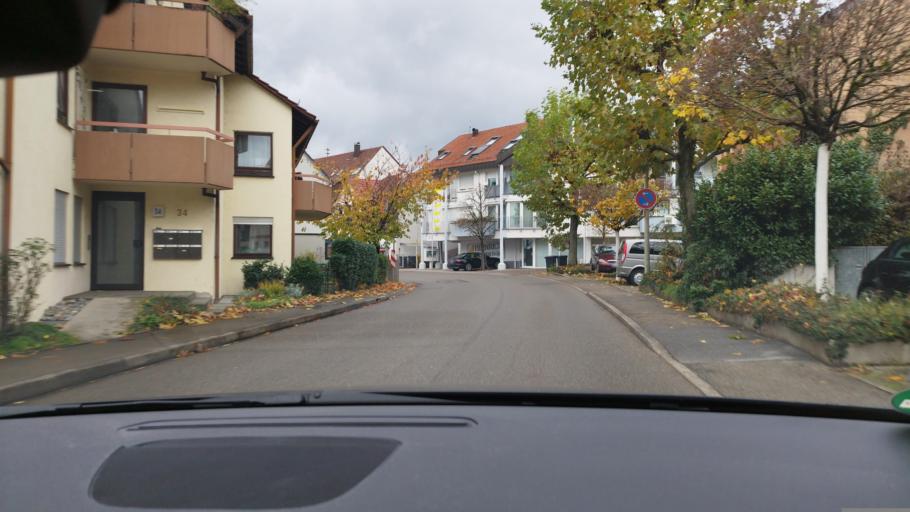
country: DE
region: Baden-Wuerttemberg
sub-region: Regierungsbezirk Stuttgart
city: Korb
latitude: 48.8418
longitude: 9.3647
